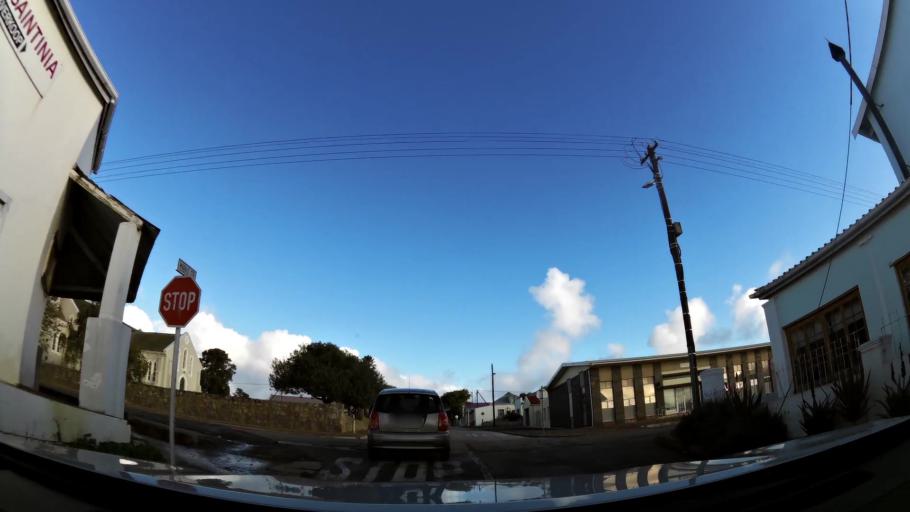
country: ZA
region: Western Cape
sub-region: Eden District Municipality
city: Riversdale
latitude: -34.2033
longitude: 21.5866
